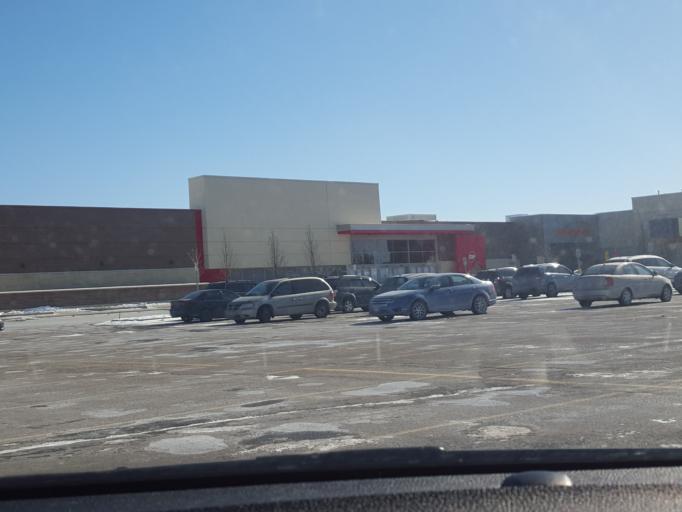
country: CA
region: Ontario
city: Waterloo
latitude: 43.4997
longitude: -80.5284
